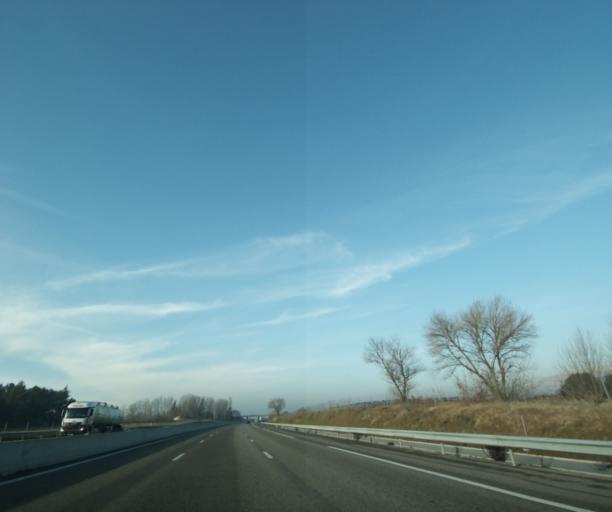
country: FR
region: Provence-Alpes-Cote d'Azur
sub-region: Departement du Var
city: Pourrieres
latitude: 43.4782
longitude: 5.7212
